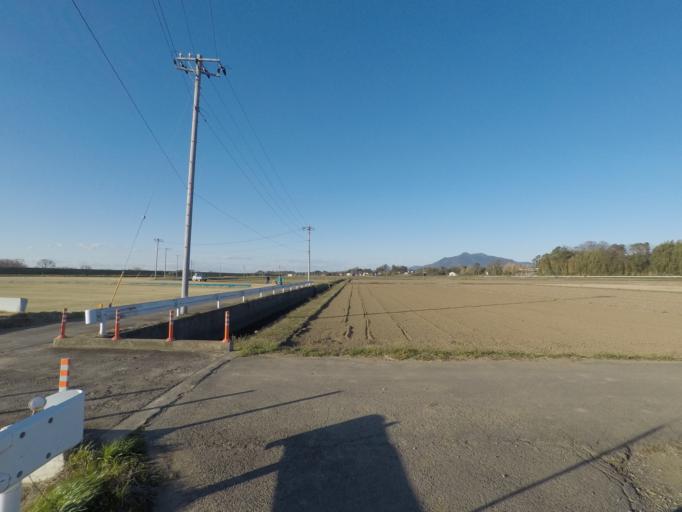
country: JP
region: Ibaraki
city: Ishige
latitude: 36.1384
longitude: 140.0034
